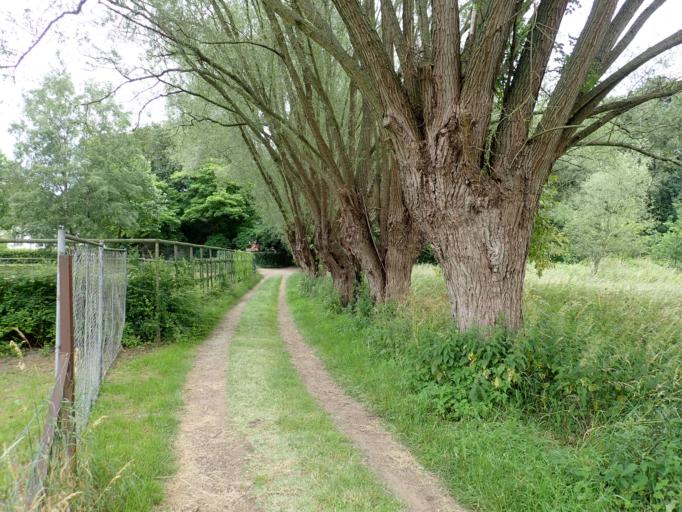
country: BE
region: Flanders
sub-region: Provincie Vlaams-Brabant
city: Keerbergen
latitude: 51.0107
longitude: 4.6201
